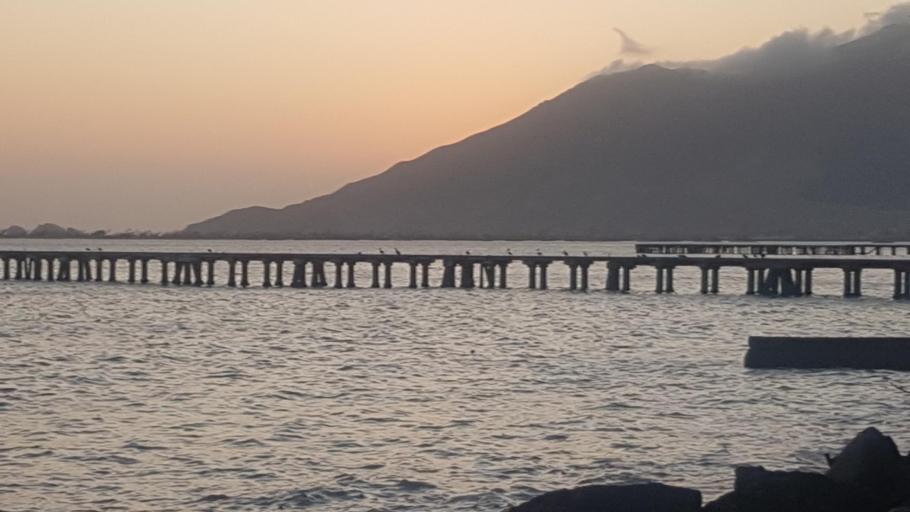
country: PE
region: Ancash
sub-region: Provincia de Santa
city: Chimbote
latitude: -9.0946
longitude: -78.5740
